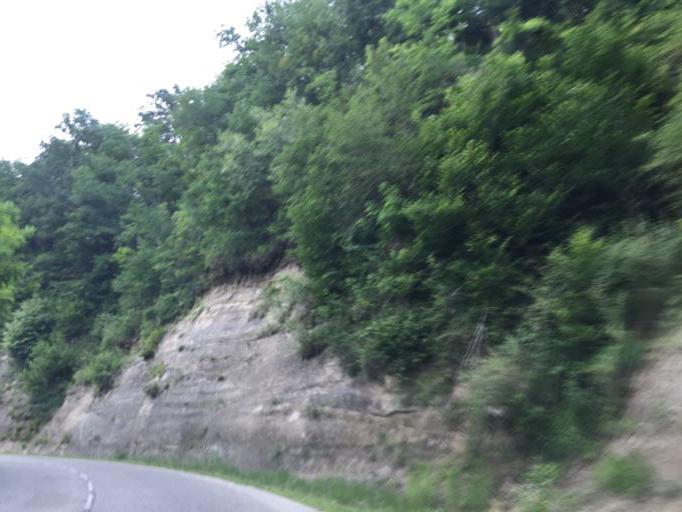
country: FR
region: Rhone-Alpes
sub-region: Departement de la Savoie
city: Le Pont-de-Beauvoisin
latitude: 45.5465
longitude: 5.6805
